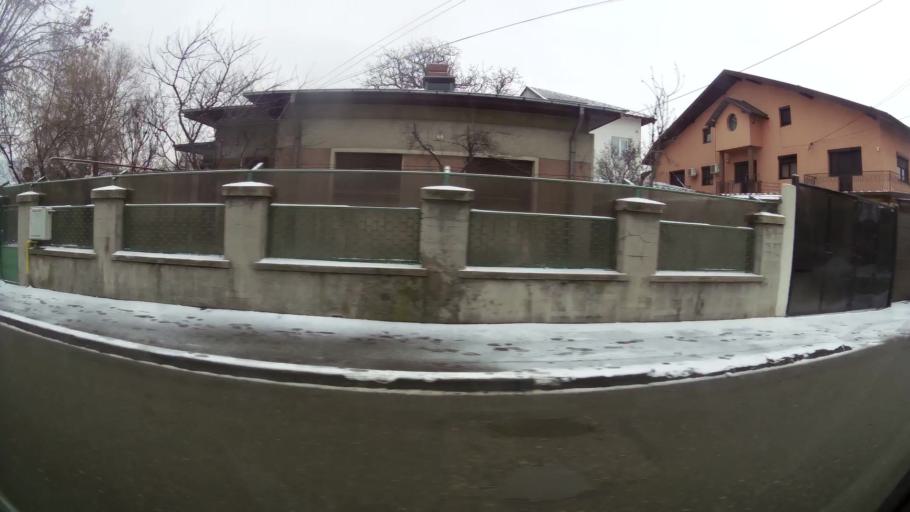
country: RO
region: Prahova
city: Ploiesti
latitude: 44.9345
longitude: 26.0427
